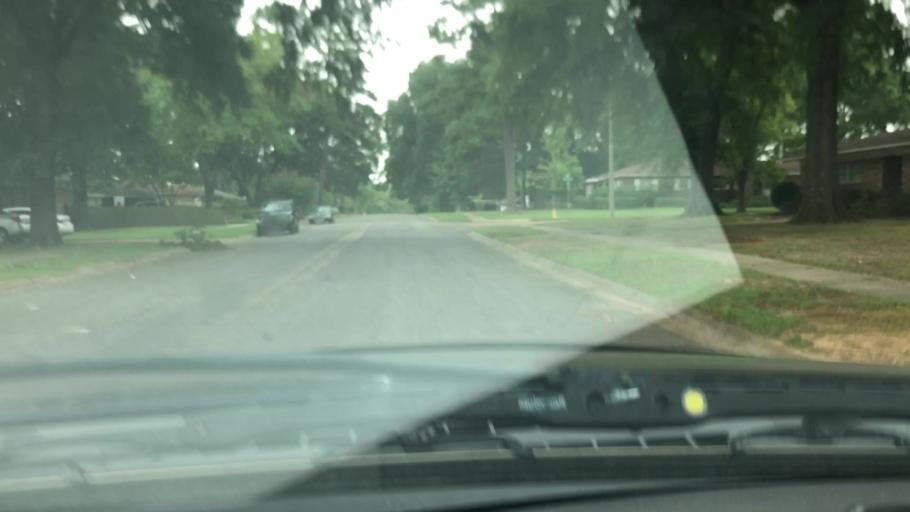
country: US
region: Arkansas
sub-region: Miller County
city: Texarkana
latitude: 33.4580
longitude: -94.0570
